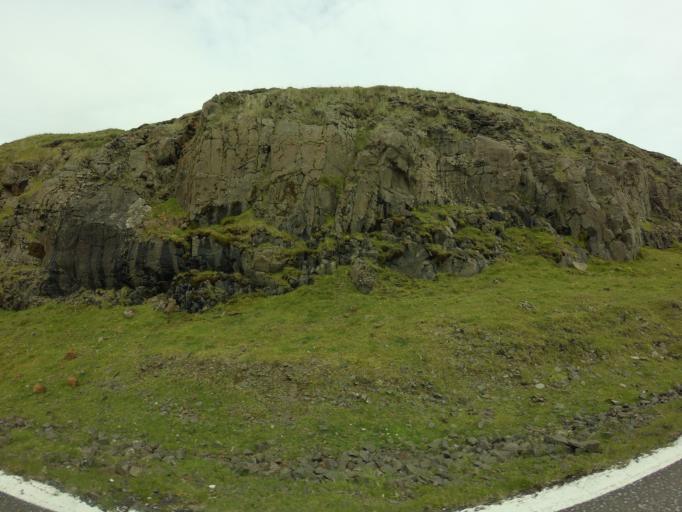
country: FO
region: Sandoy
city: Sandur
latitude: 61.8228
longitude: -6.7156
